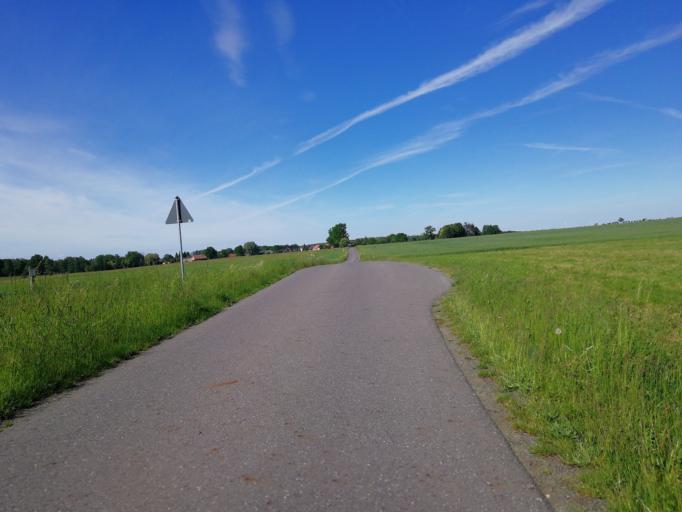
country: DE
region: Brandenburg
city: Calau
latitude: 51.7380
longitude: 13.9181
